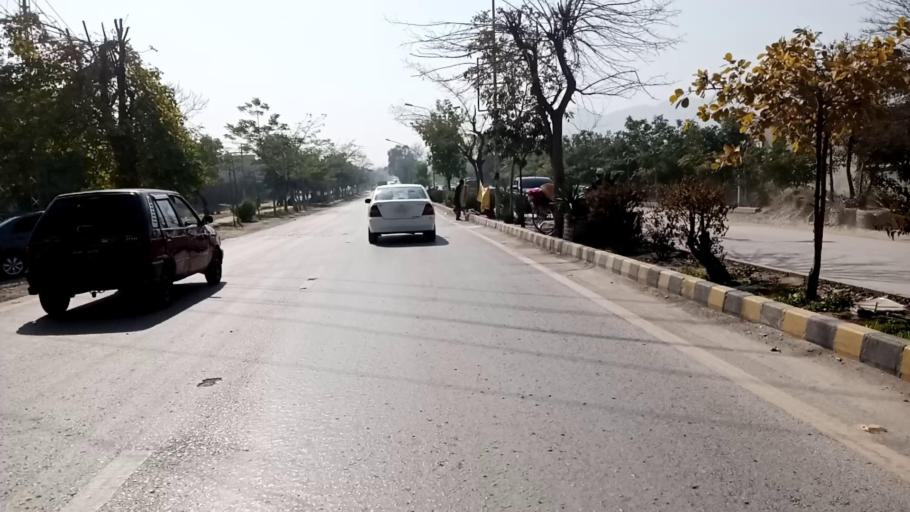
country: PK
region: Khyber Pakhtunkhwa
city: Peshawar
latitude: 33.9611
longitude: 71.4330
